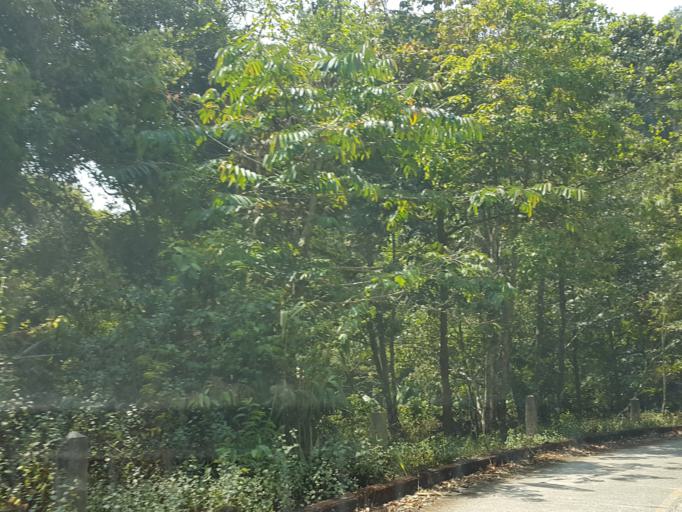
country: TH
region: Chiang Mai
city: Mae On
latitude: 18.8406
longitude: 99.3754
